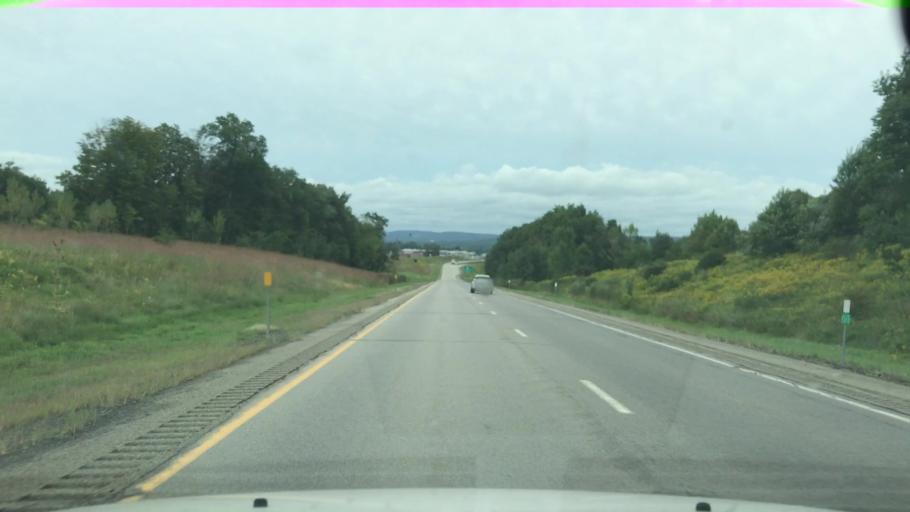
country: US
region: New York
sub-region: Erie County
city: Springville
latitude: 42.5195
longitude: -78.6971
